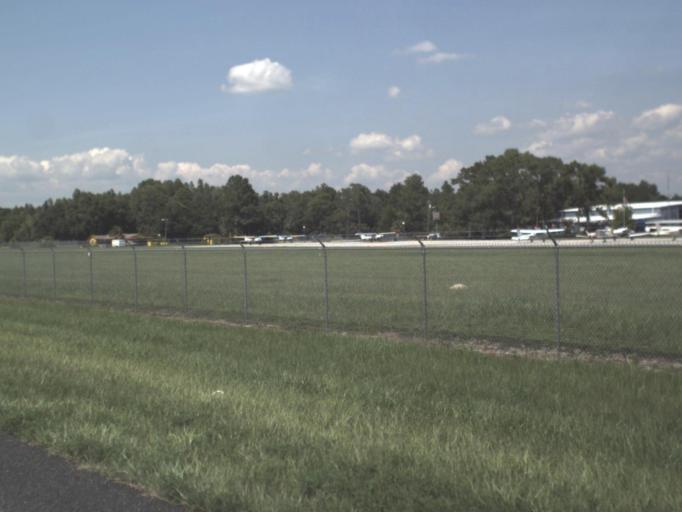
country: US
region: Florida
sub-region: Citrus County
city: Crystal River
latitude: 28.8700
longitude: -82.5796
